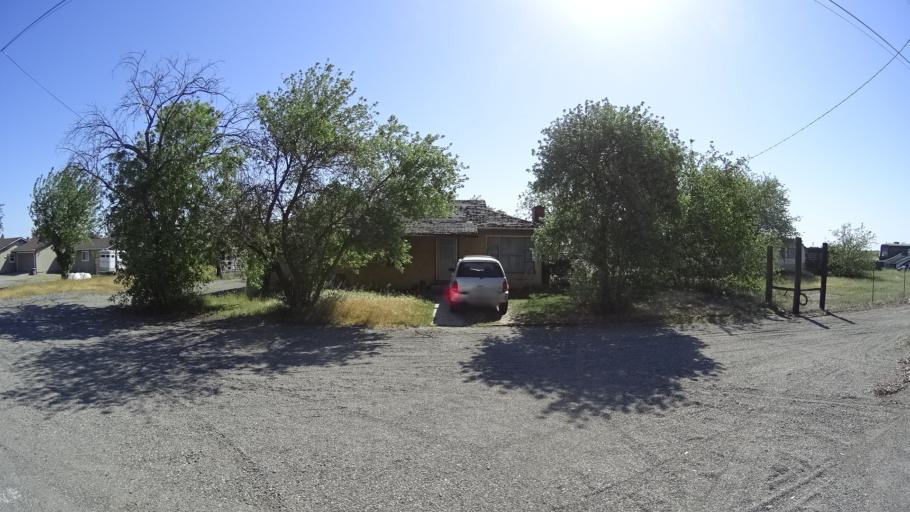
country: US
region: California
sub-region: Glenn County
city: Orland
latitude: 39.7252
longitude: -122.1690
